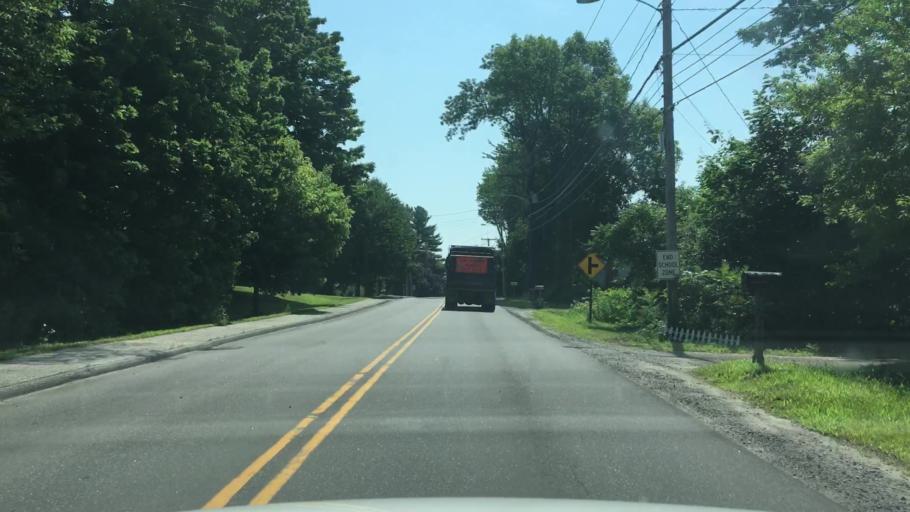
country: US
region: Maine
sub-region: Kennebec County
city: Hallowell
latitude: 44.2928
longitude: -69.7997
